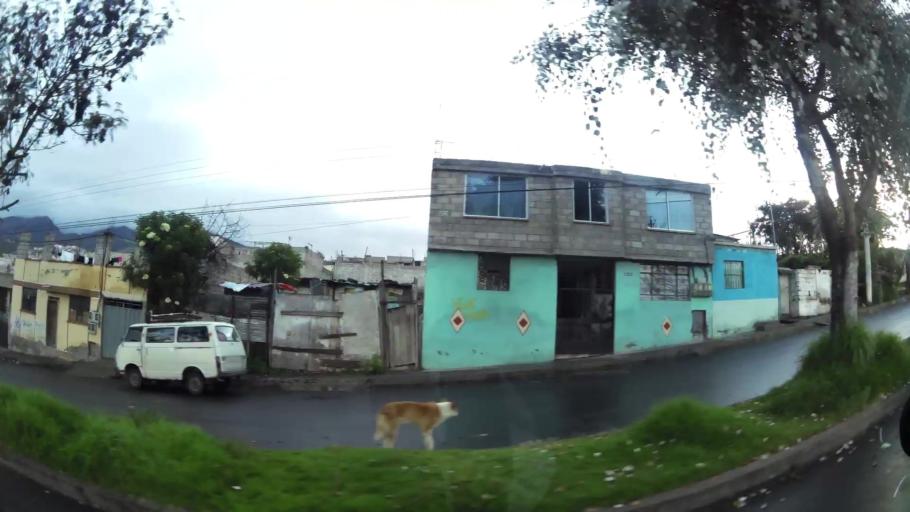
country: EC
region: Pichincha
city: Quito
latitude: -0.0892
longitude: -78.5125
